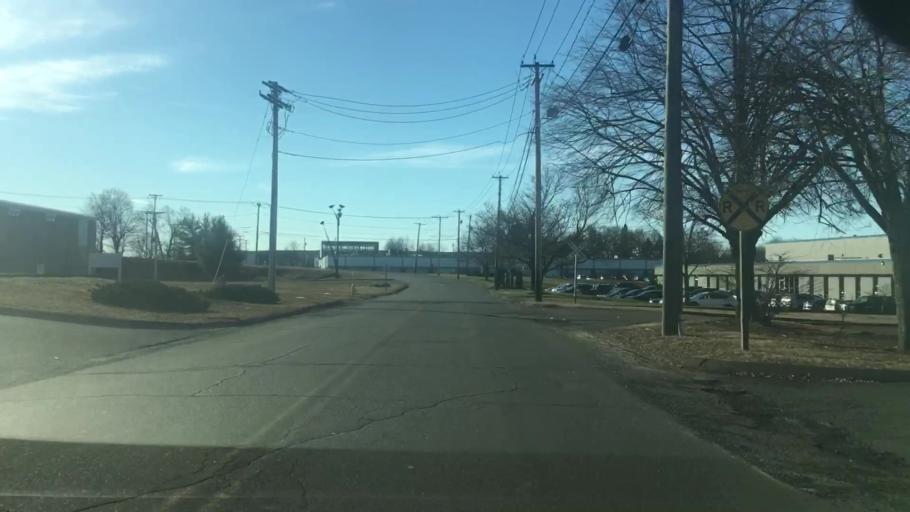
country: US
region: Connecticut
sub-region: New Haven County
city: North Haven
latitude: 41.4201
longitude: -72.8442
